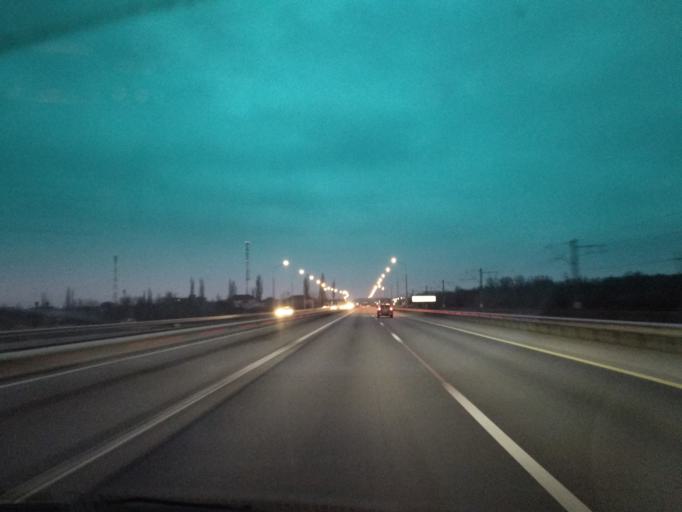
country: RU
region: Adygeya
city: Adygeysk
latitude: 44.8078
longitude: 39.2291
